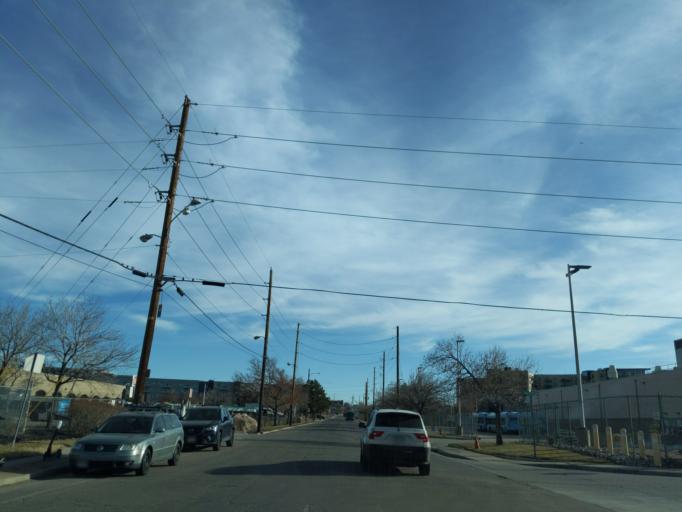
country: US
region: Colorado
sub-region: Denver County
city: Denver
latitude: 39.7693
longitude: -104.9872
